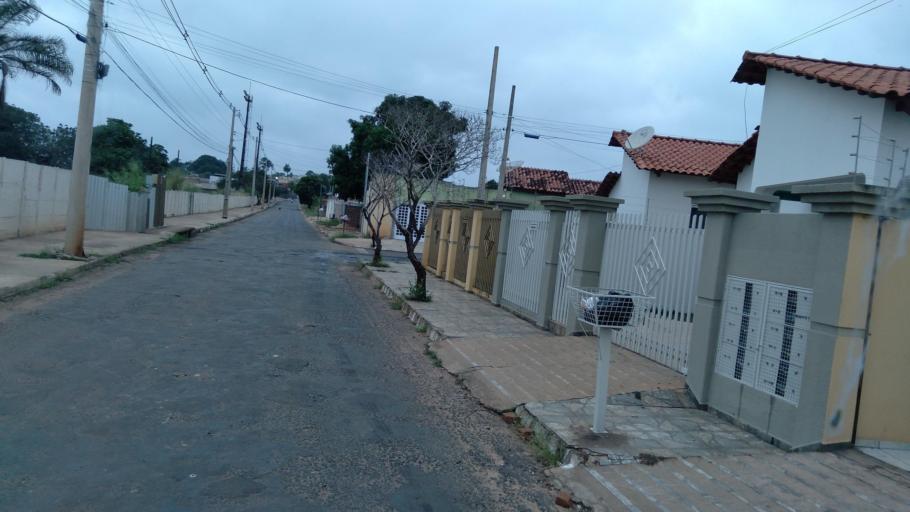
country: BR
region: Goias
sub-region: Mineiros
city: Mineiros
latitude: -17.5749
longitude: -52.5483
